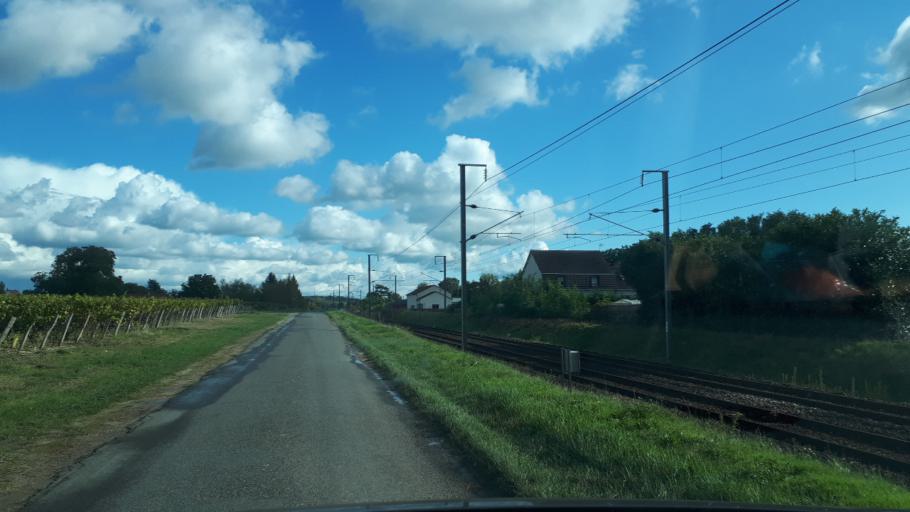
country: FR
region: Centre
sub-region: Departement du Loir-et-Cher
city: Thesee
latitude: 47.3179
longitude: 1.3246
